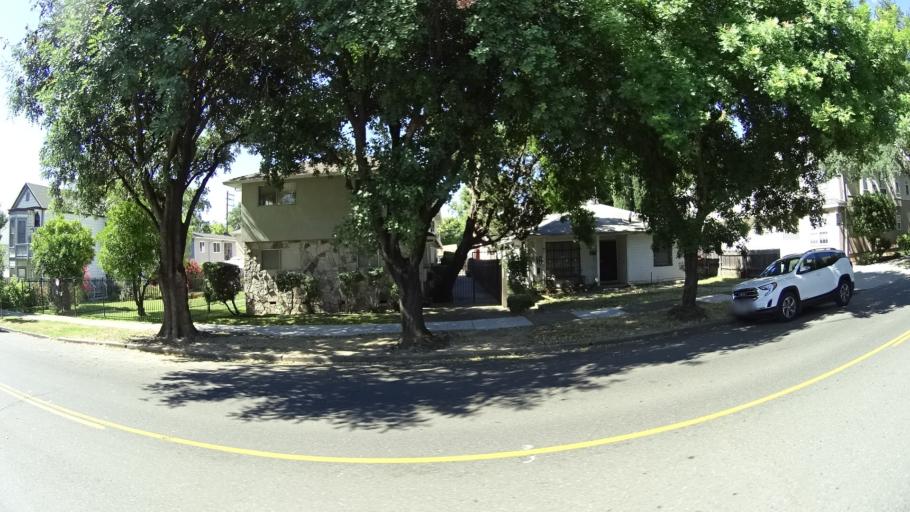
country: US
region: California
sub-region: Sacramento County
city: Sacramento
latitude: 38.5659
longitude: -121.4809
